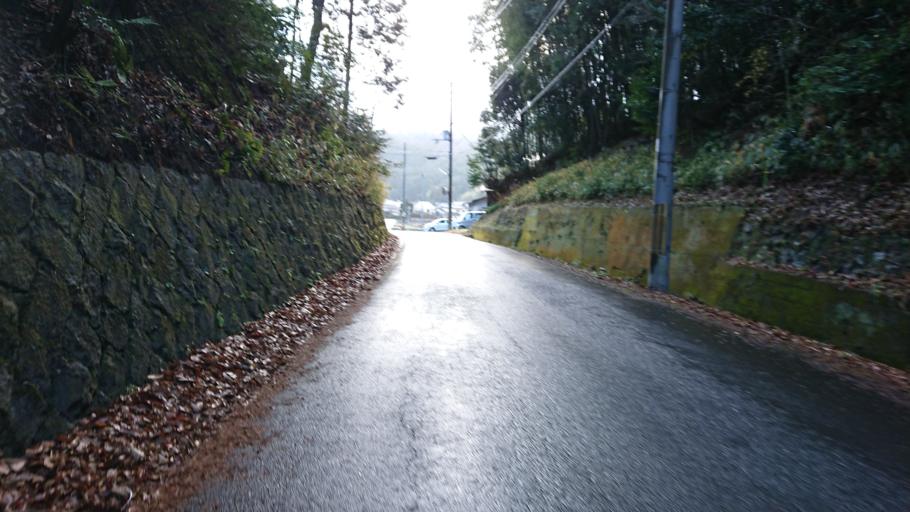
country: JP
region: Kyoto
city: Kameoka
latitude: 35.0503
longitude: 135.5169
